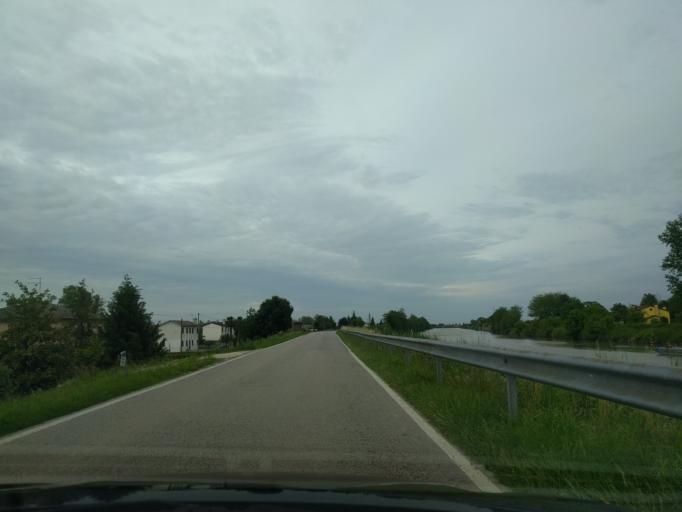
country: IT
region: Veneto
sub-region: Provincia di Rovigo
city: Villanova Marchesana
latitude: 45.0492
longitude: 11.9847
